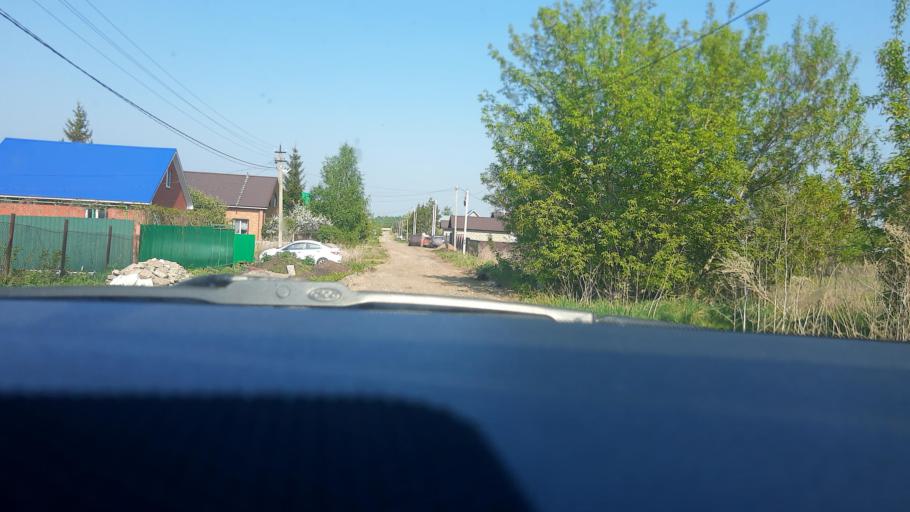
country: RU
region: Bashkortostan
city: Avdon
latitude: 54.5484
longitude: 55.7704
